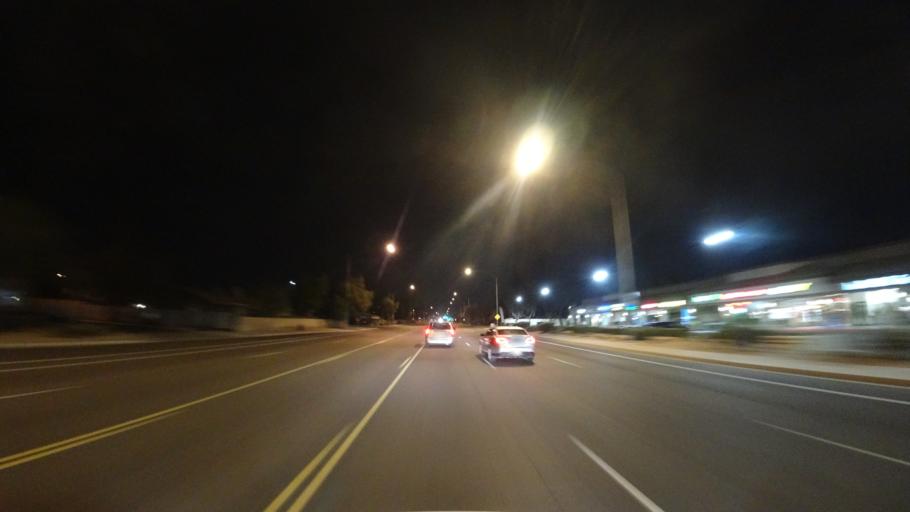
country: US
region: Arizona
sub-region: Maricopa County
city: Mesa
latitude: 33.4070
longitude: -111.7712
